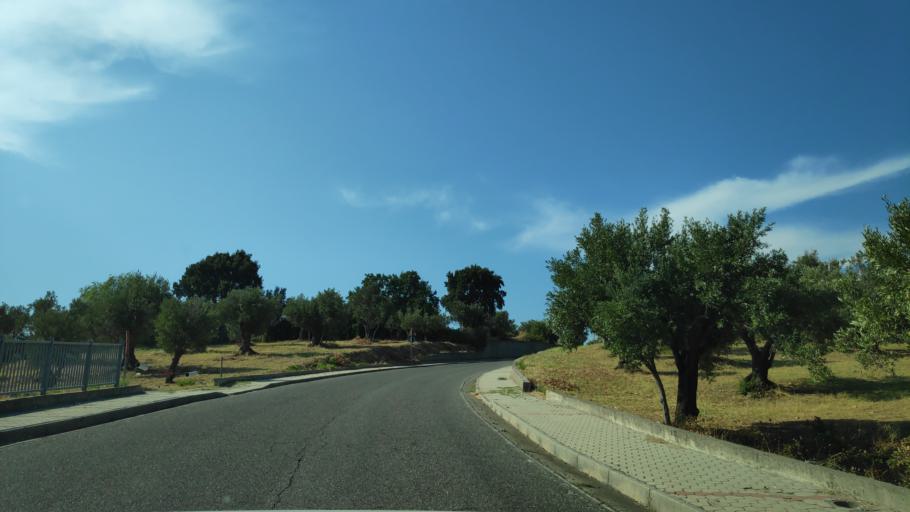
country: IT
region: Calabria
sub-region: Provincia di Catanzaro
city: Soverato Superiore
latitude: 38.6861
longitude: 16.5369
